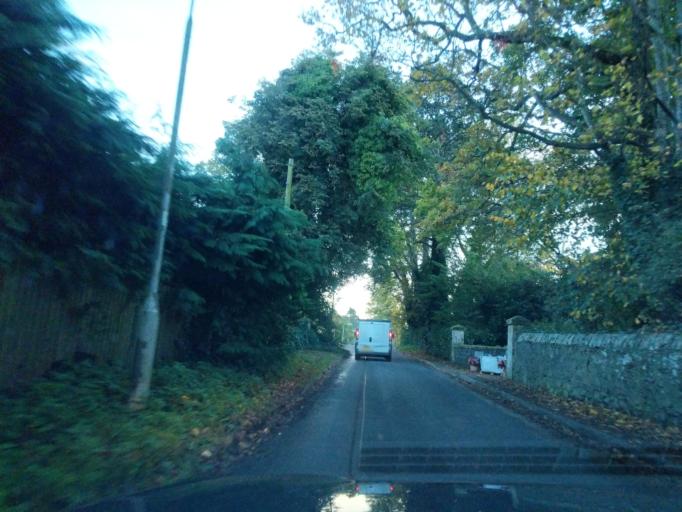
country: GB
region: Scotland
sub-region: Fife
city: Leuchars
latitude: 56.3864
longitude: -2.8777
